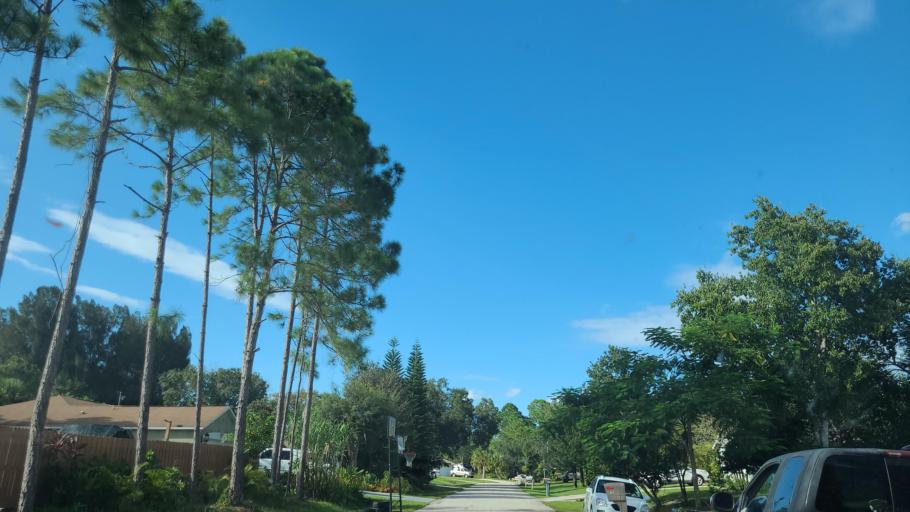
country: US
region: Florida
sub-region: Brevard County
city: June Park
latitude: 27.9825
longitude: -80.6710
